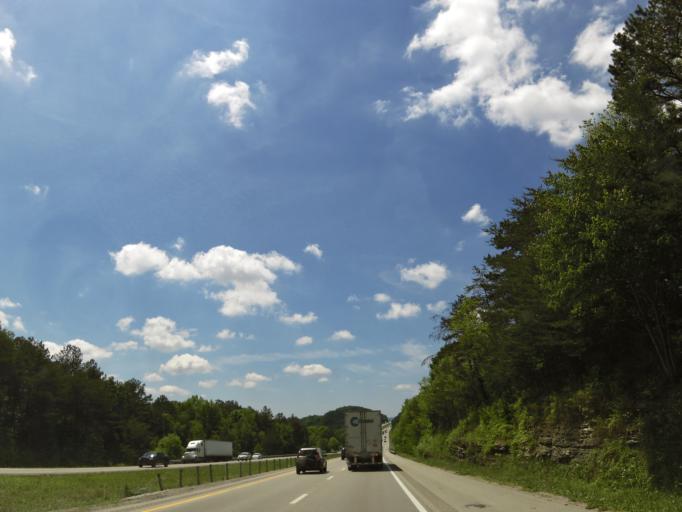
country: US
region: Kentucky
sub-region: Whitley County
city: Williamsburg
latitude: 36.8234
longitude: -84.1650
